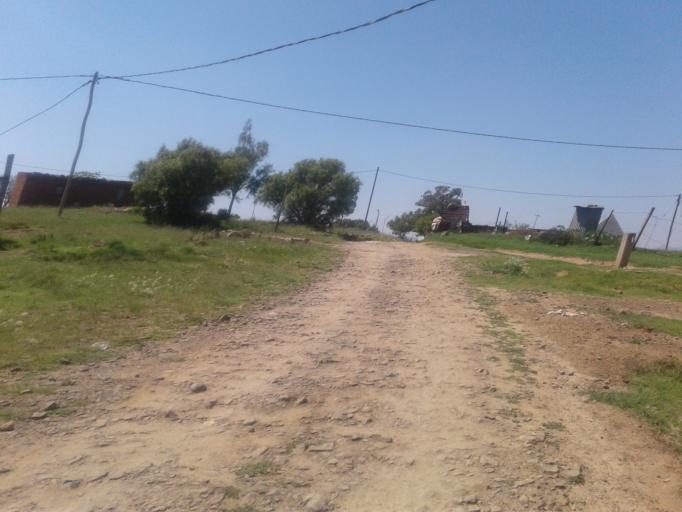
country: LS
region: Mafeteng
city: Mafeteng
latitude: -29.7550
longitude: 27.1102
